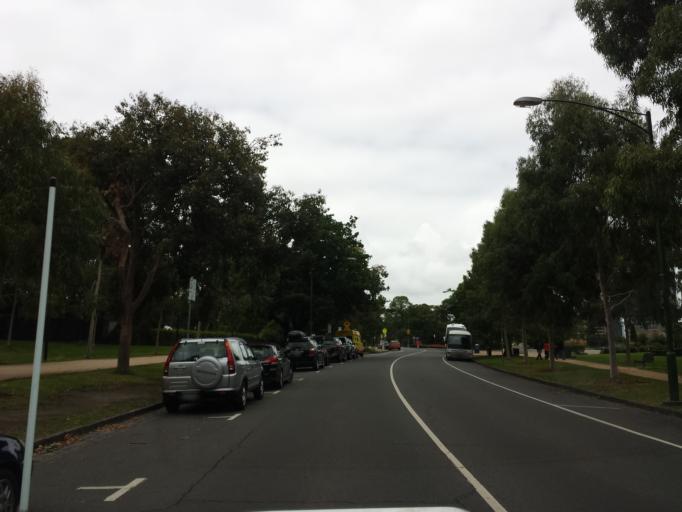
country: AU
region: Victoria
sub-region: Port Phillip
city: South Melbourne
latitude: -37.8289
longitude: 144.9741
